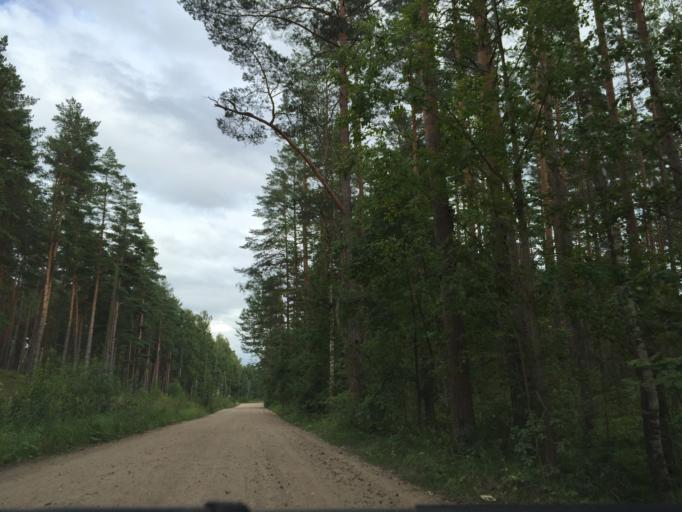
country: LV
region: Saulkrastu
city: Saulkrasti
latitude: 57.1909
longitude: 24.3588
